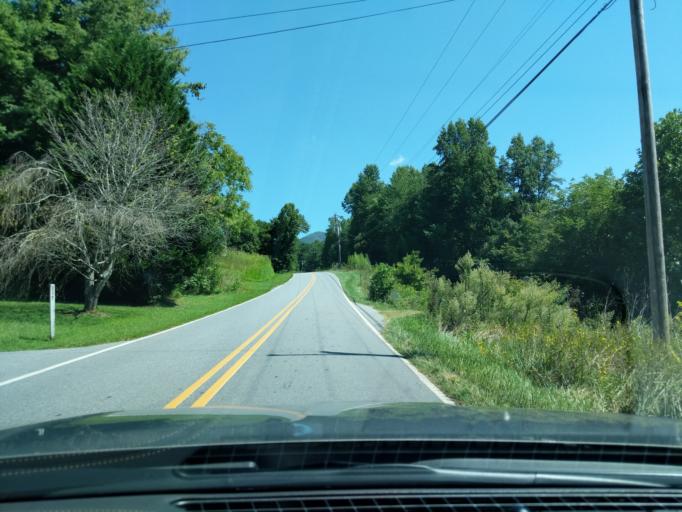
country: US
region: Georgia
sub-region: Towns County
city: Hiawassee
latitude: 35.0304
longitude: -83.7352
